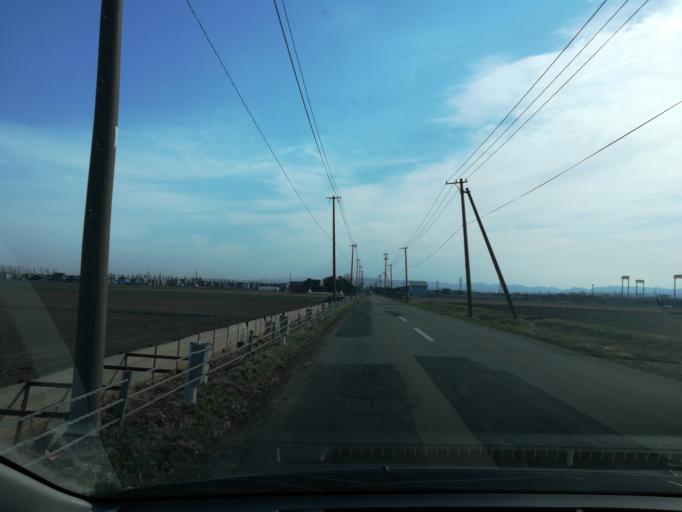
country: JP
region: Hokkaido
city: Iwamizawa
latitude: 43.1998
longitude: 141.7335
